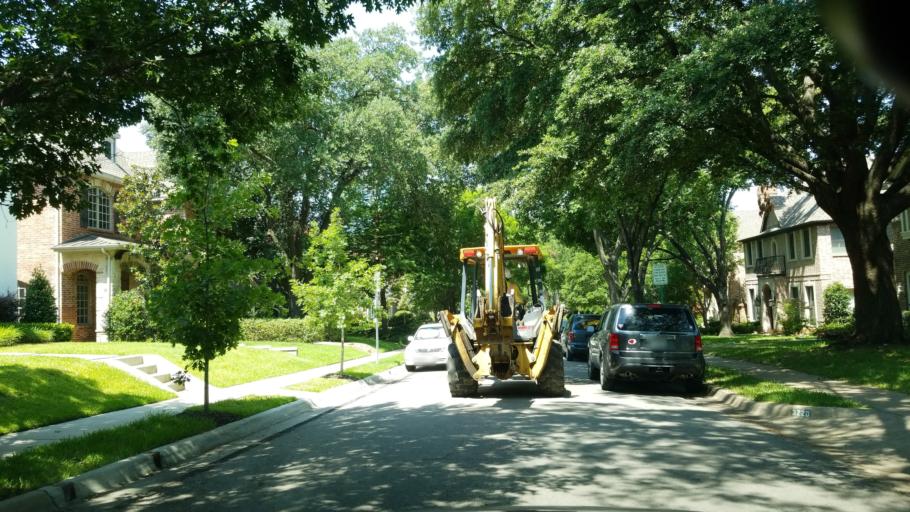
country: US
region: Texas
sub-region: Dallas County
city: University Park
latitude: 32.8493
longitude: -96.7838
